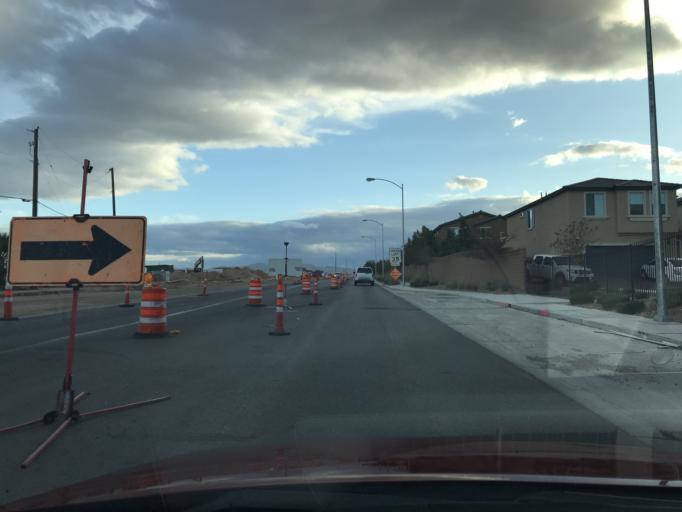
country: US
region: Nevada
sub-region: Clark County
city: Enterprise
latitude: 36.0331
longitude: -115.2790
